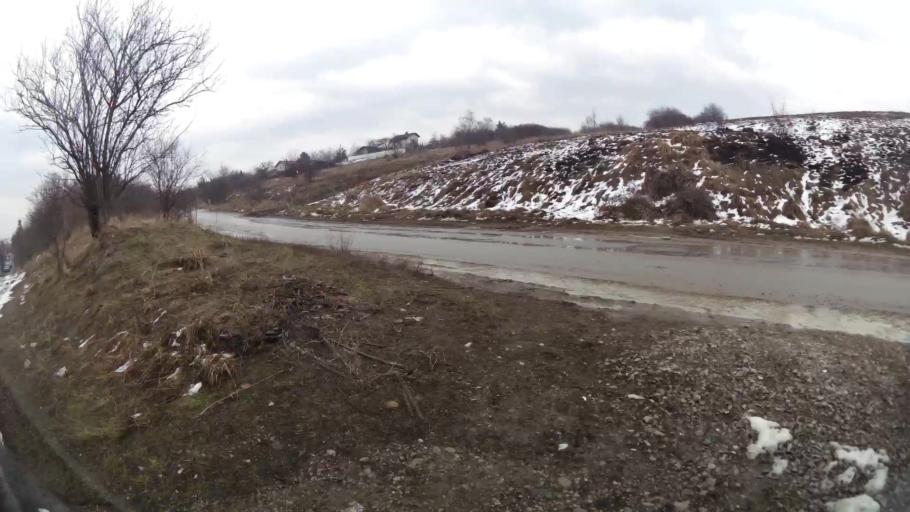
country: BG
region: Sofiya
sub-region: Obshtina Bozhurishte
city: Bozhurishte
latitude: 42.6940
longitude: 23.2179
